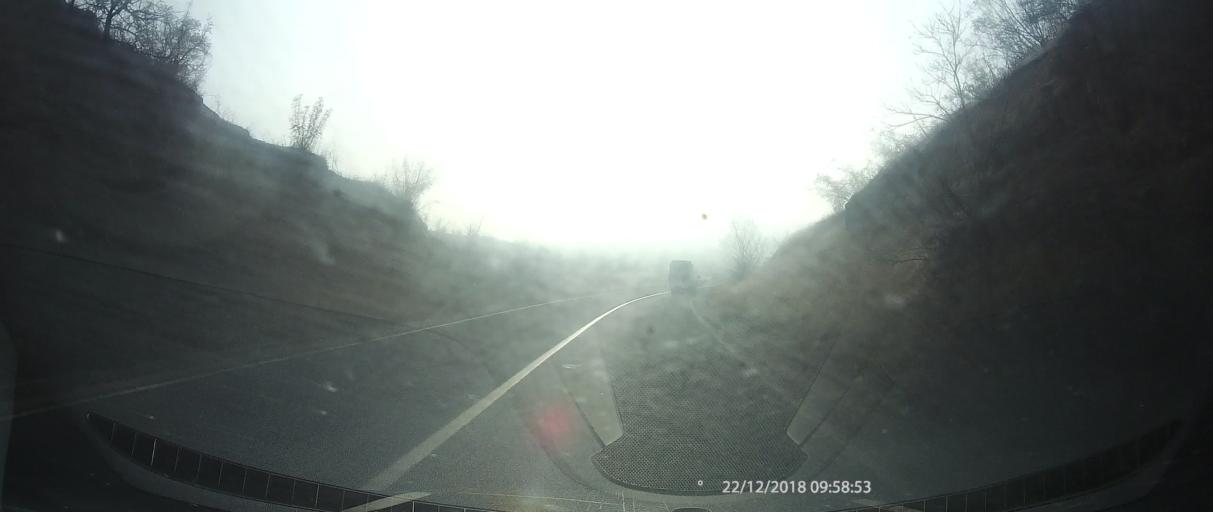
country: MK
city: Klechovce
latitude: 42.1554
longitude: 21.9506
